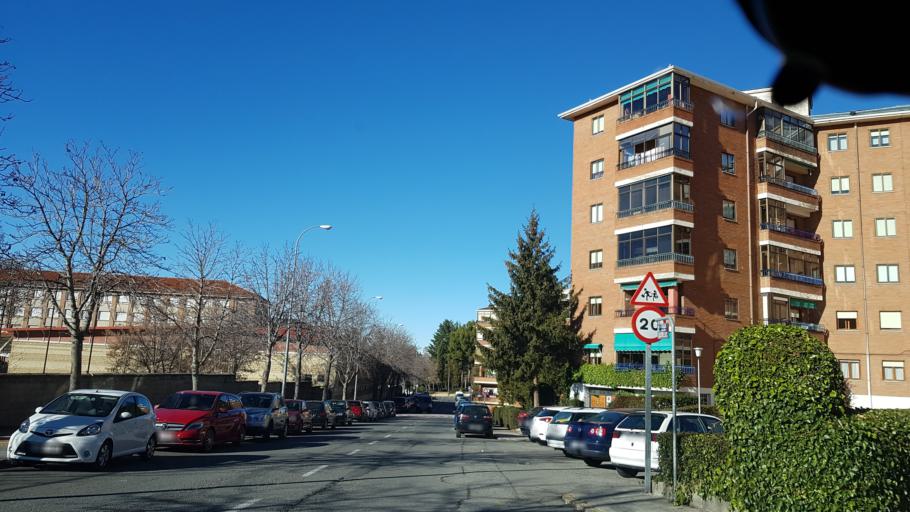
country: ES
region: Castille and Leon
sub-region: Provincia de Segovia
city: Segovia
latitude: 40.9454
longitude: -4.1094
